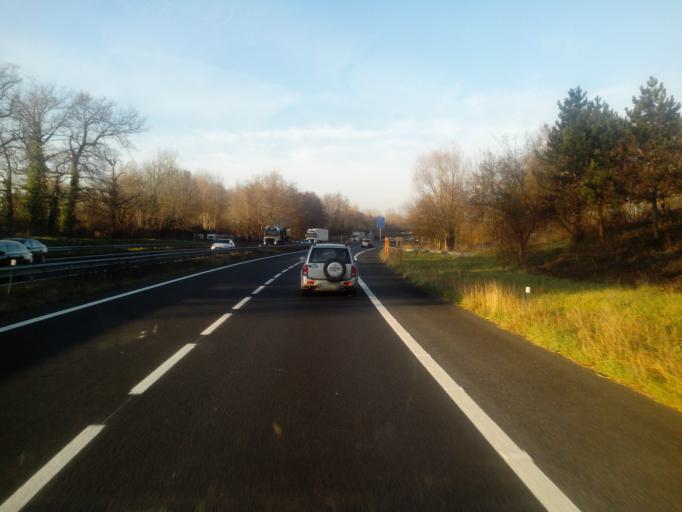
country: FR
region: Limousin
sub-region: Departement de la Correze
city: Saint-Pantaleon-de-Larche
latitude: 45.1420
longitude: 1.4871
